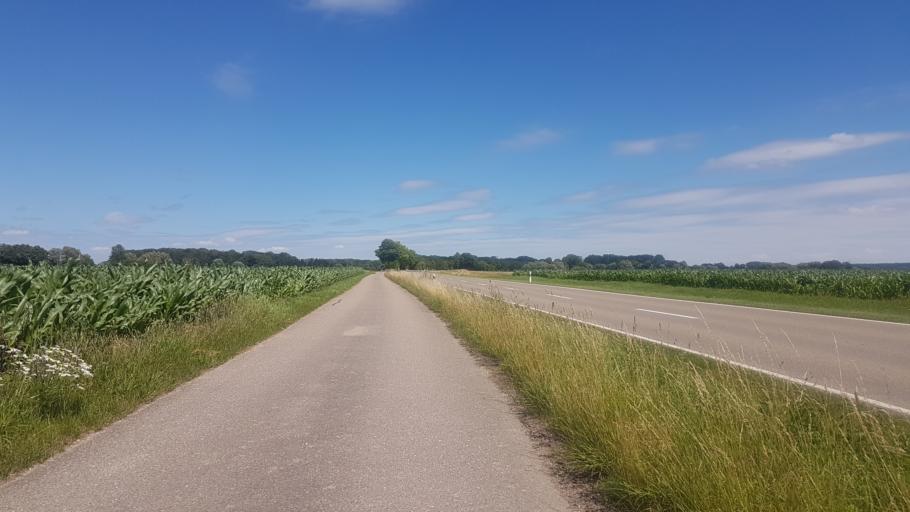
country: DE
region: Bavaria
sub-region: Swabia
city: Schwenningen
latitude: 48.6289
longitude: 10.6628
